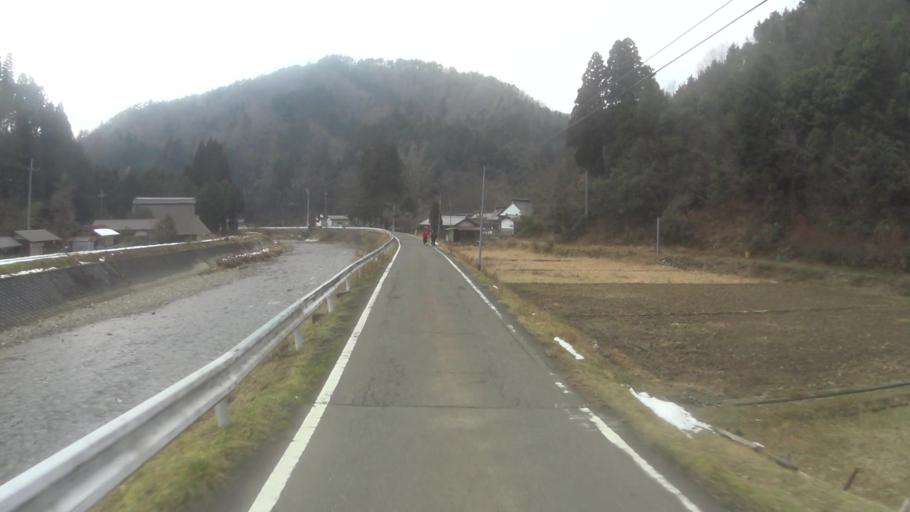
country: JP
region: Kyoto
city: Maizuru
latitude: 35.3987
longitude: 135.4810
